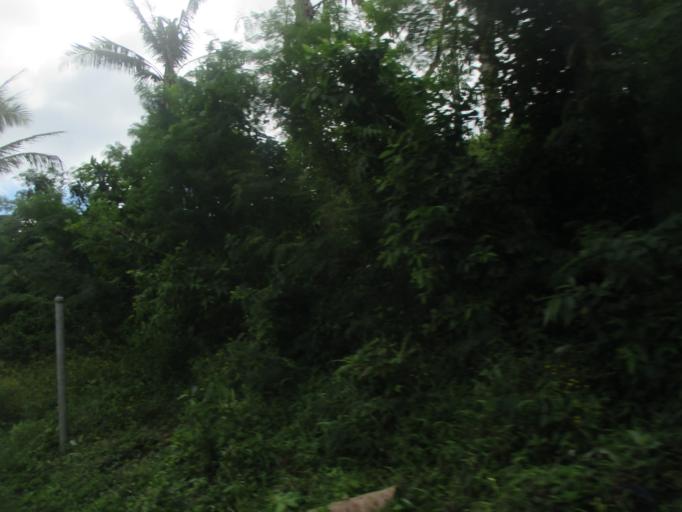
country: PH
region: Eastern Visayas
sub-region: Province of Eastern Samar
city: Lawa-an
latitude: 11.1074
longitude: 125.2092
